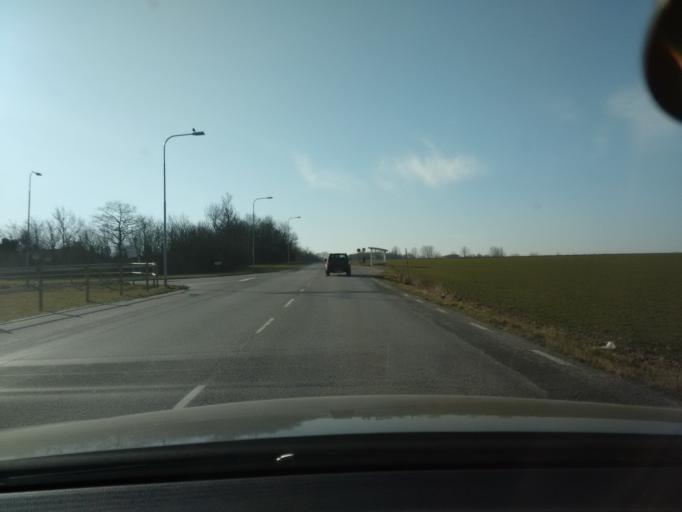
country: SE
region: Skane
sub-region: Lunds Kommun
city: Lund
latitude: 55.7381
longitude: 13.1741
